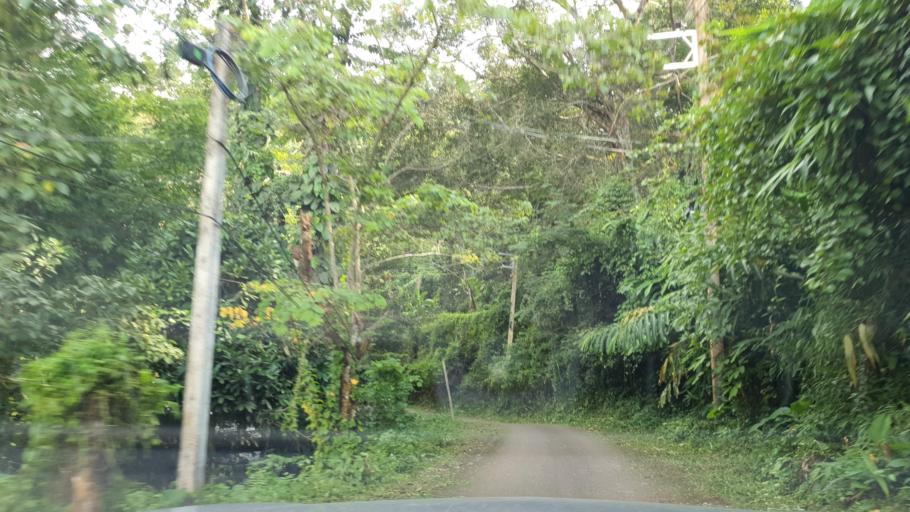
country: TH
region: Chiang Mai
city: Mae On
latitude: 18.9245
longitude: 99.3145
